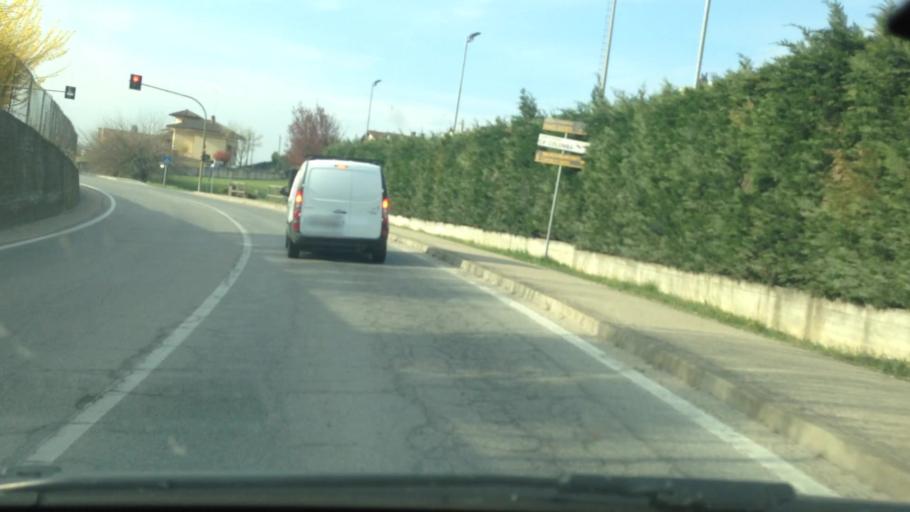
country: IT
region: Piedmont
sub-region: Provincia di Asti
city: San Damiano d'Asti
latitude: 44.8325
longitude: 8.0601
